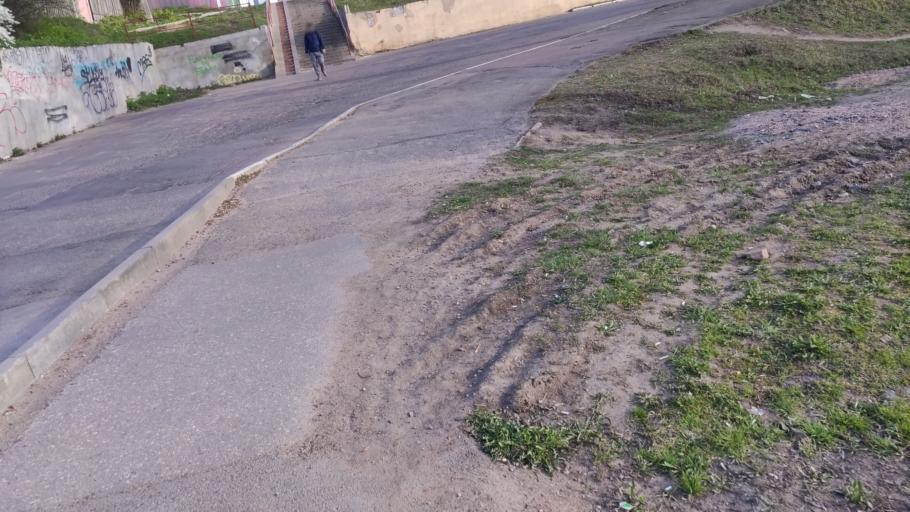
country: BY
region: Minsk
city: Minsk
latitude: 53.9000
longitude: 27.5169
